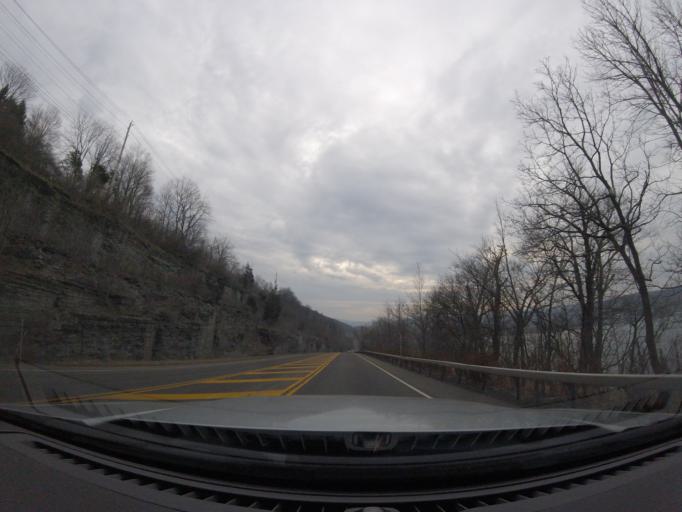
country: US
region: New York
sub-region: Schuyler County
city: Watkins Glen
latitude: 42.3940
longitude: -76.8567
